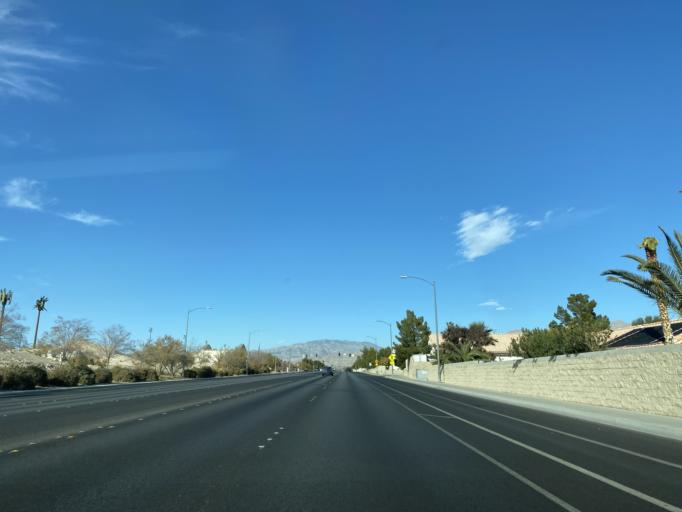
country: US
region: Nevada
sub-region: Clark County
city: Las Vegas
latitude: 36.2848
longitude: -115.2604
